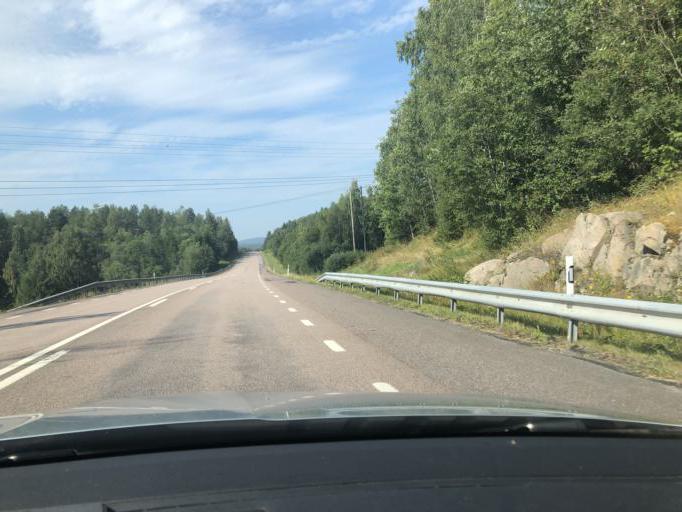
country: SE
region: Vaesternorrland
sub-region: Haernoesands Kommun
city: Haernoesand
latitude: 62.7933
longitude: 17.9006
